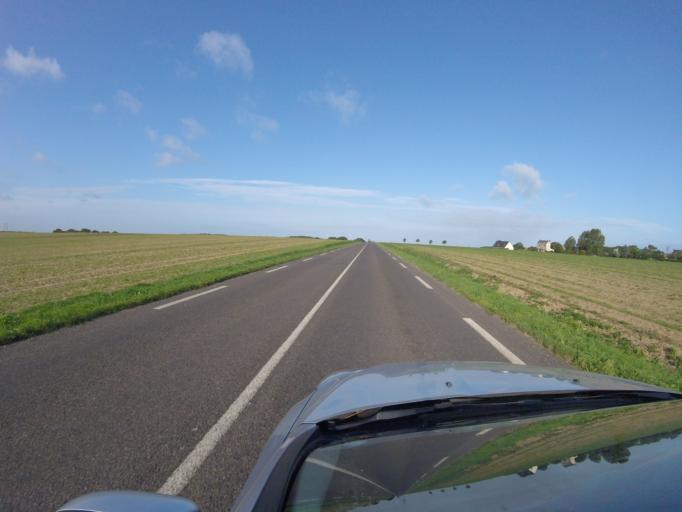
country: FR
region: Haute-Normandie
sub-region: Departement de la Seine-Maritime
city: Fecamp
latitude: 49.7673
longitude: 0.4136
